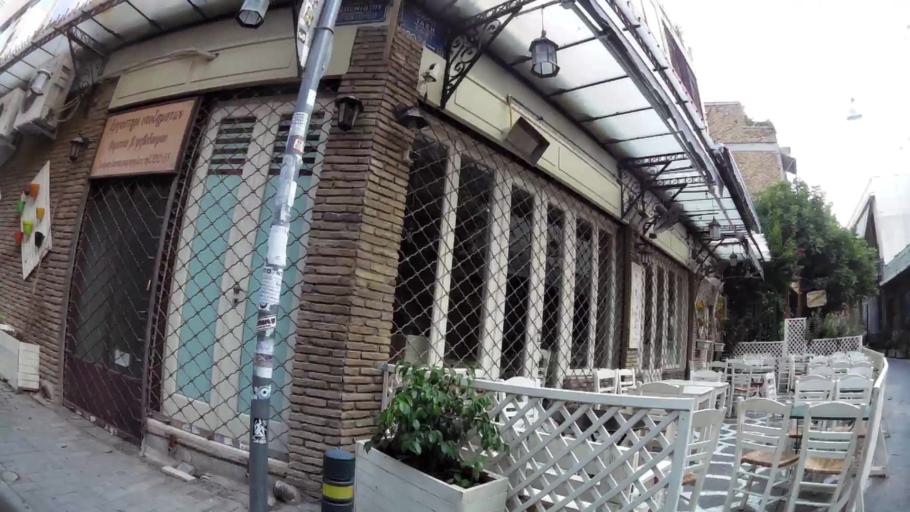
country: GR
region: Attica
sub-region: Nomarchia Athinas
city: Athens
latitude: 37.9782
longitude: 23.7235
